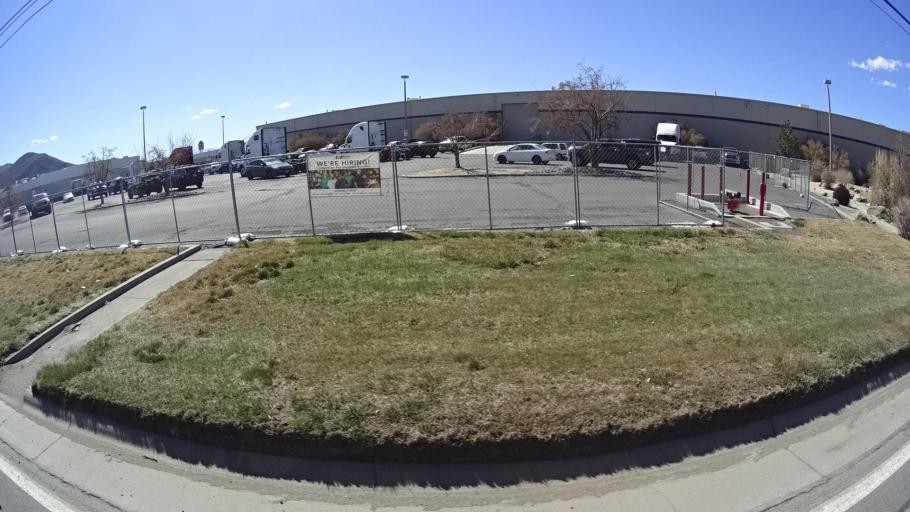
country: US
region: Nevada
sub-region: Washoe County
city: Sparks
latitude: 39.5304
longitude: -119.7029
